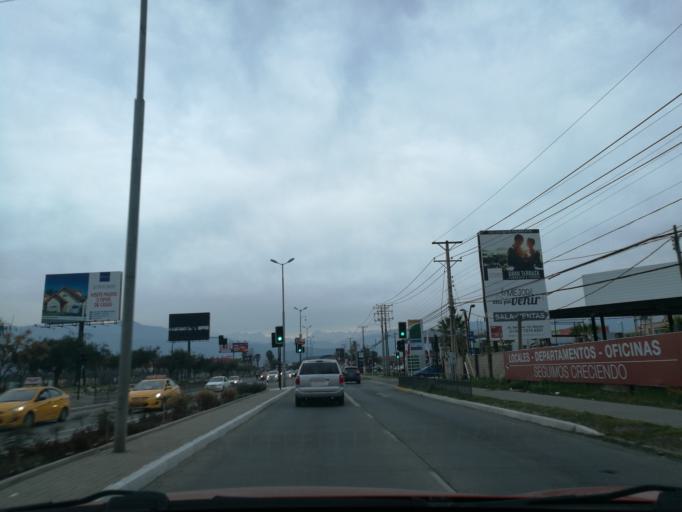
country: CL
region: O'Higgins
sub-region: Provincia de Cachapoal
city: Rancagua
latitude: -34.1759
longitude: -70.7006
